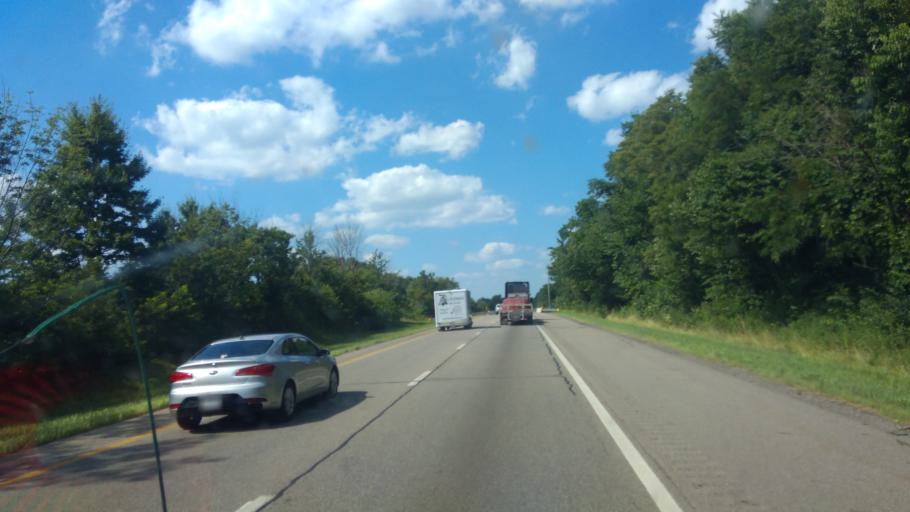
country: US
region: Ohio
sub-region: Stark County
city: Richville
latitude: 40.6929
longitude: -81.4314
